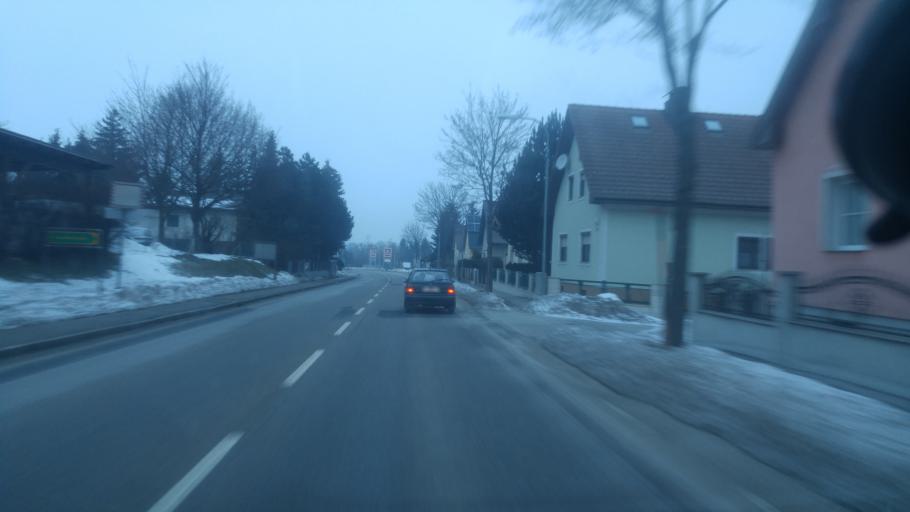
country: AT
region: Lower Austria
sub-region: Politischer Bezirk Lilienfeld
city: Hainfeld
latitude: 48.0387
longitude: 15.7618
